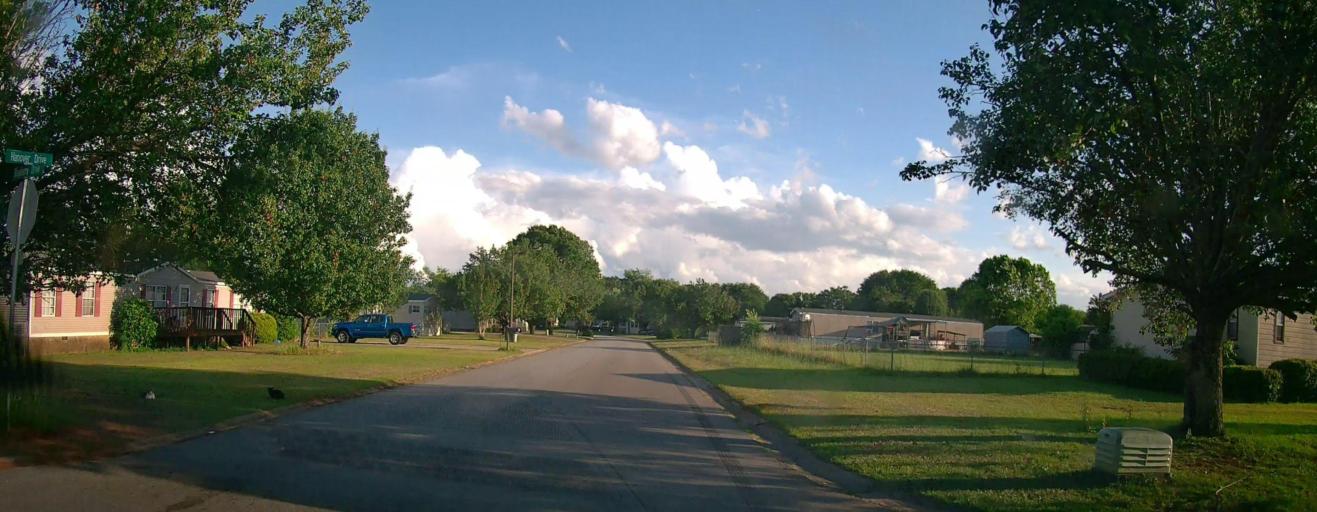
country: US
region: Georgia
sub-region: Houston County
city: Centerville
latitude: 32.6386
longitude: -83.7242
